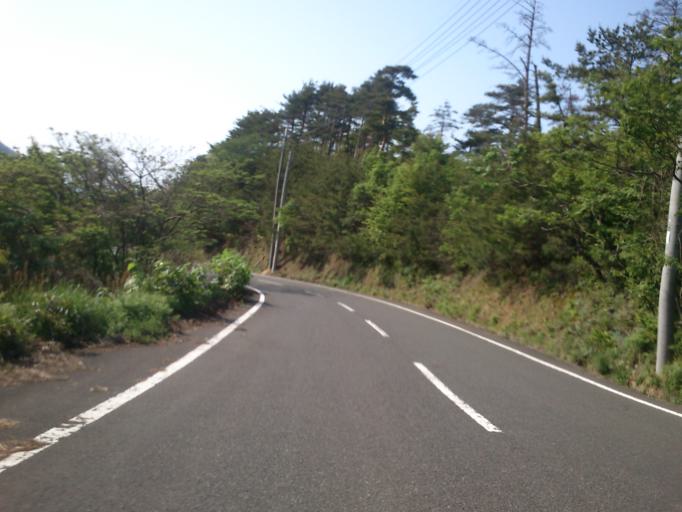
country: JP
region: Kyoto
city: Miyazu
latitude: 35.7387
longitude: 135.1756
